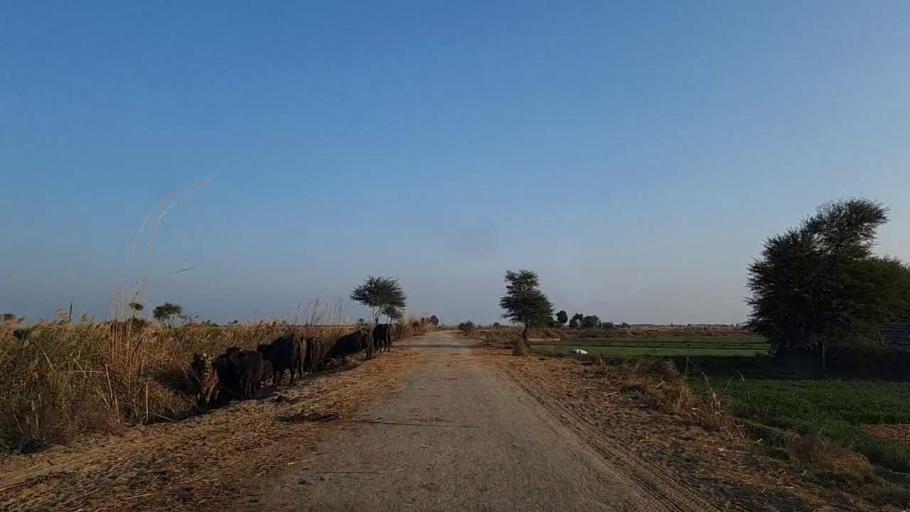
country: PK
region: Sindh
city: Sanghar
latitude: 26.2750
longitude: 68.9814
